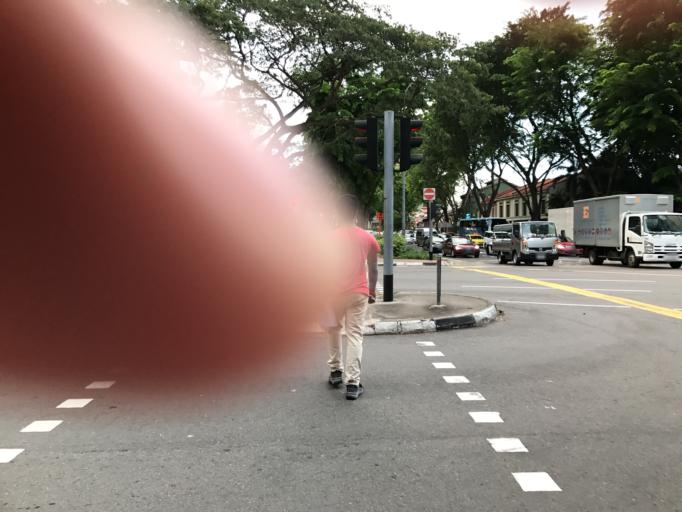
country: SG
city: Singapore
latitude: 1.2996
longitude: 103.8592
